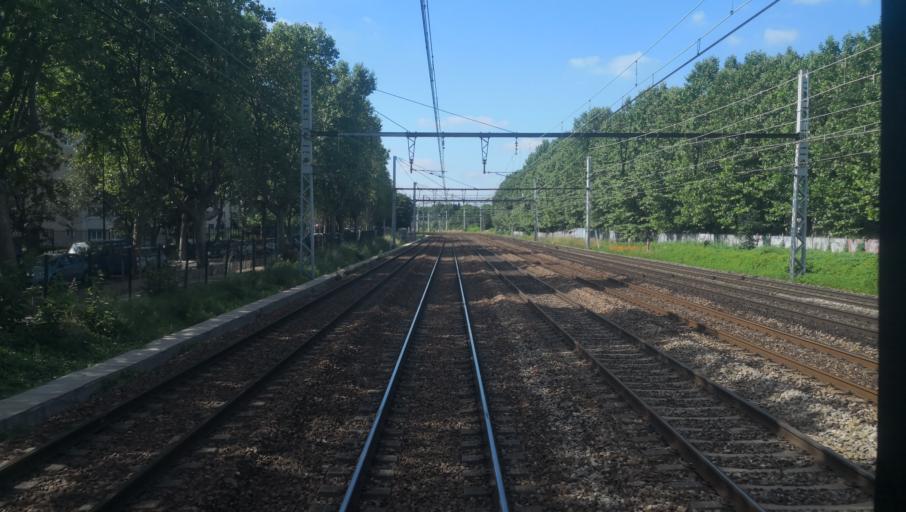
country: FR
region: Ile-de-France
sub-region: Departement du Val-de-Marne
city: Alfortville
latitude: 48.8057
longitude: 2.4250
